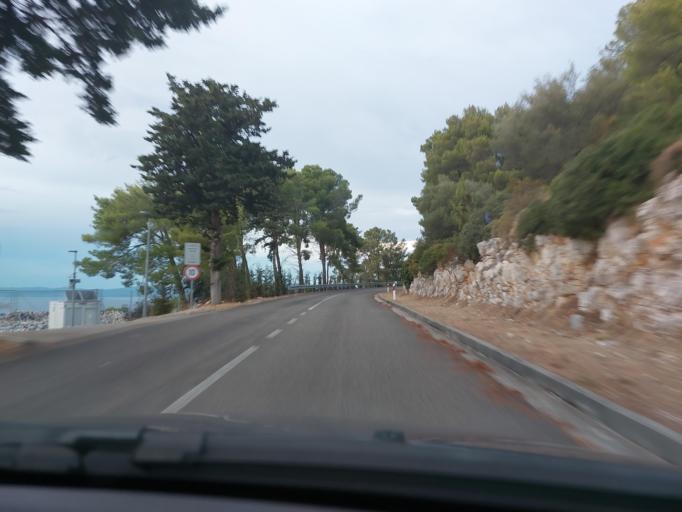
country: HR
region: Dubrovacko-Neretvanska
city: Smokvica
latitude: 42.7684
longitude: 16.8539
